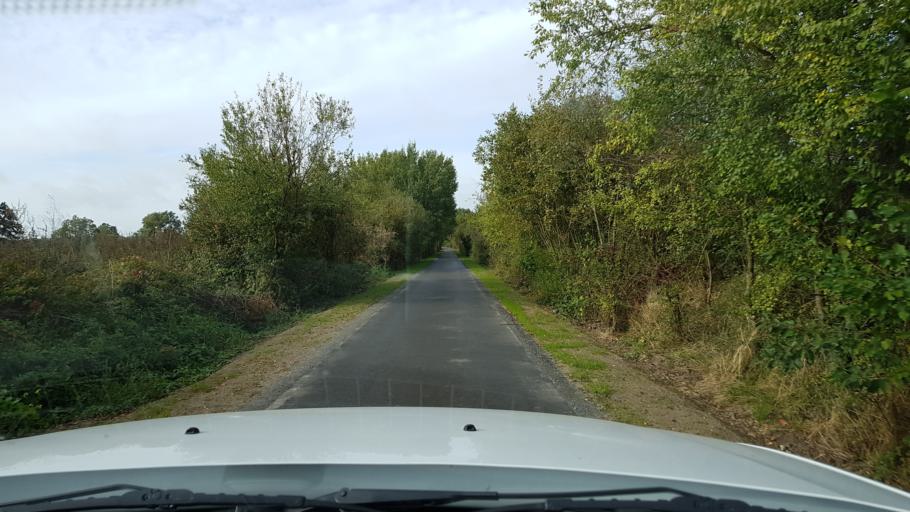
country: PL
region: West Pomeranian Voivodeship
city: Trzcinsko Zdroj
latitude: 52.9534
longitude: 14.5872
